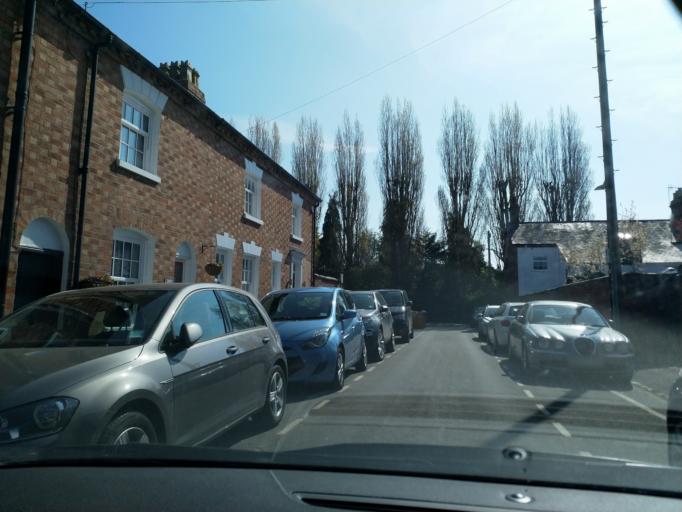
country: GB
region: England
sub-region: Warwickshire
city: Stratford-upon-Avon
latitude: 52.1863
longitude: -1.7094
